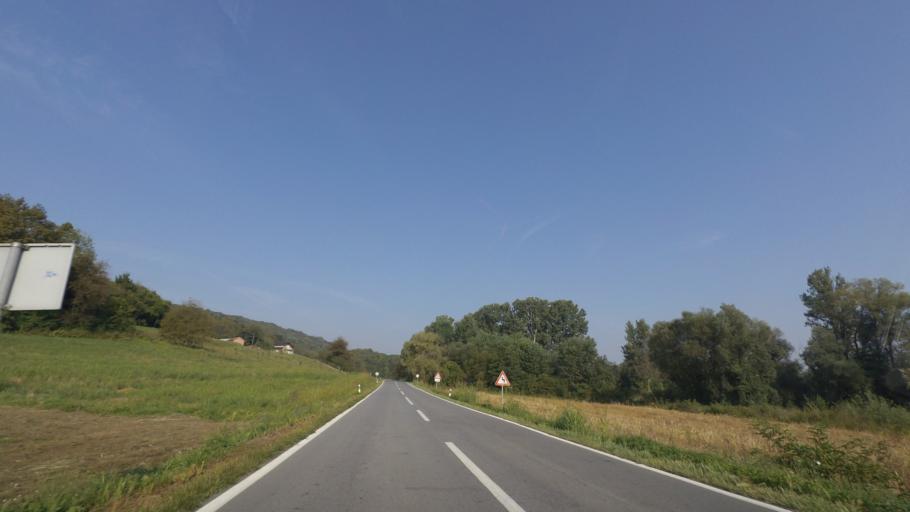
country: HR
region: Pozesko-Slavonska
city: Pozega
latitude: 45.3488
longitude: 17.5633
